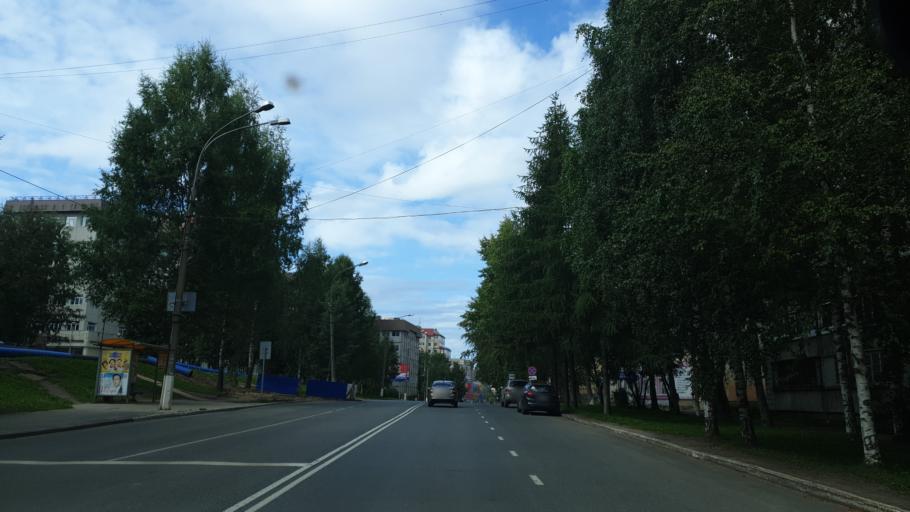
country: RU
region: Komi Republic
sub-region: Syktyvdinskiy Rayon
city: Syktyvkar
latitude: 61.6699
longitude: 50.8264
